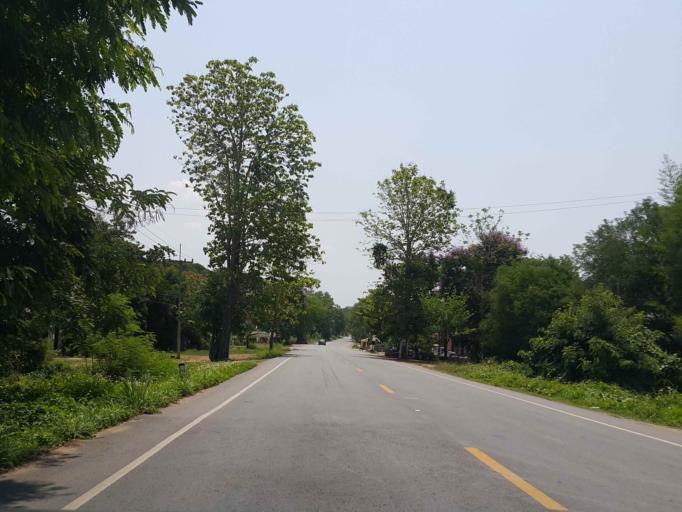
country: TH
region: Chiang Mai
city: Mae Taeng
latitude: 19.1120
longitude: 99.0200
